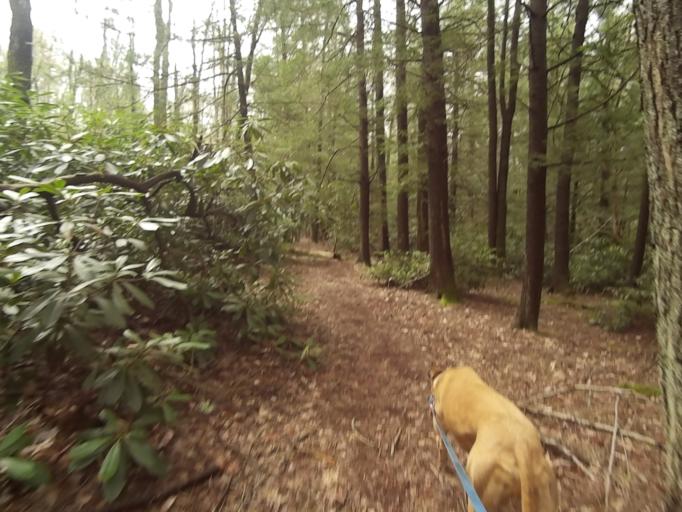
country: US
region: Pennsylvania
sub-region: Centre County
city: Boalsburg
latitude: 40.7356
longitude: -77.7558
